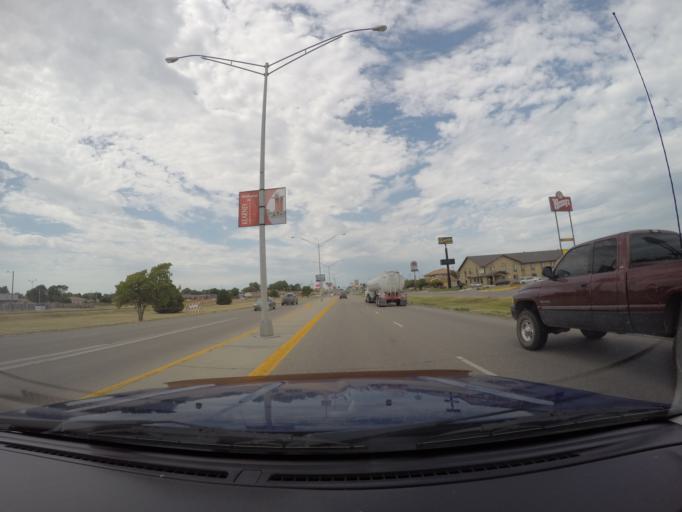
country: US
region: Nebraska
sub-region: Buffalo County
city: Kearney
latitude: 40.6828
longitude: -99.0844
